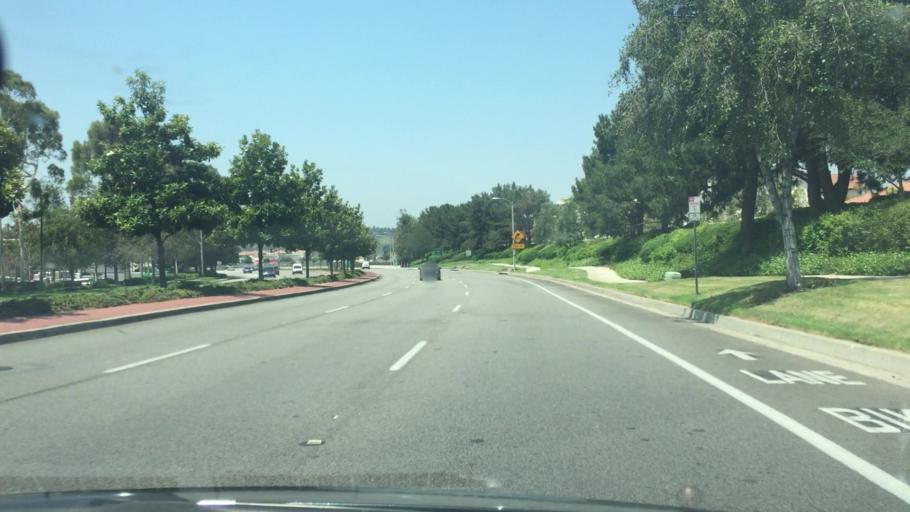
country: US
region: California
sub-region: Orange County
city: Rancho Santa Margarita
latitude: 33.6438
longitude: -117.6002
